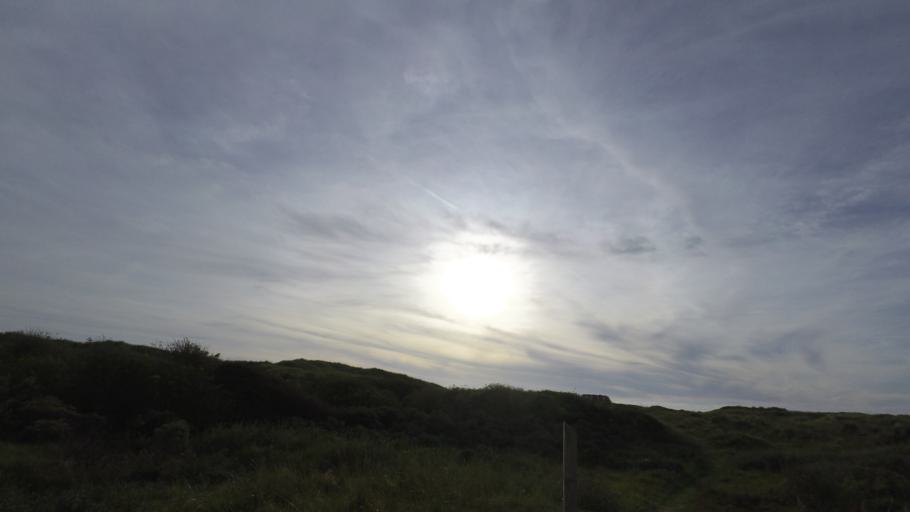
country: NL
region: Friesland
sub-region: Gemeente Ameland
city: Nes
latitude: 53.4600
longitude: 5.8127
